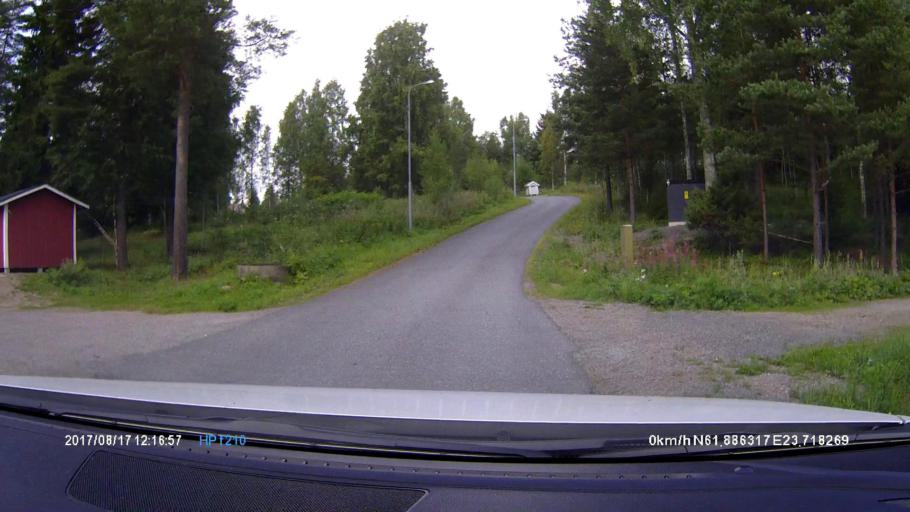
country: FI
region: Pirkanmaa
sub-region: Tampere
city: Kuru
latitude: 61.8865
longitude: 23.7179
